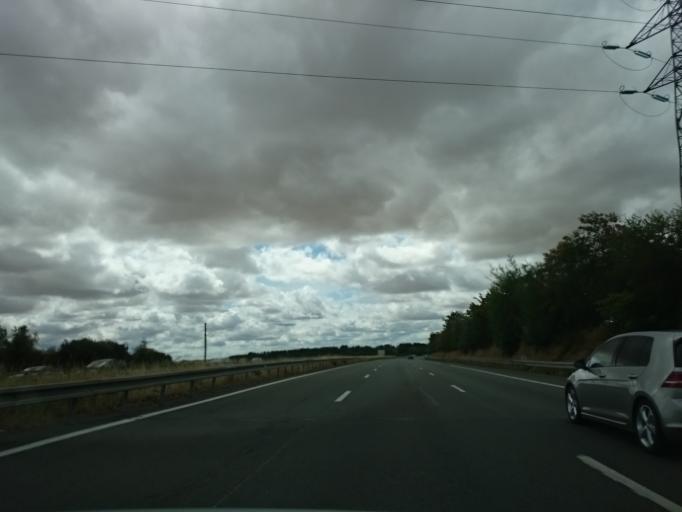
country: FR
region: Centre
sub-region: Departement d'Eure-et-Loir
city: Morancez
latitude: 48.3892
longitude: 1.4931
